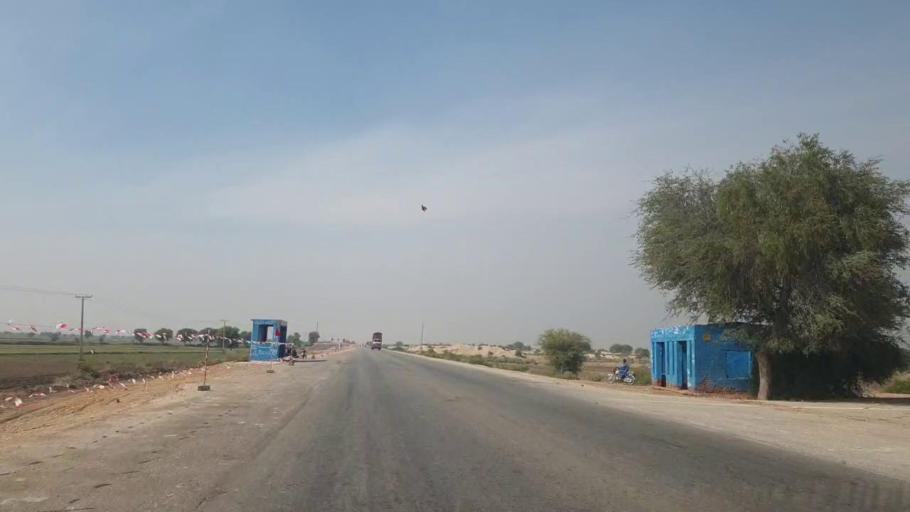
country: PK
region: Sindh
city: Sann
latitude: 25.9902
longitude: 68.1761
